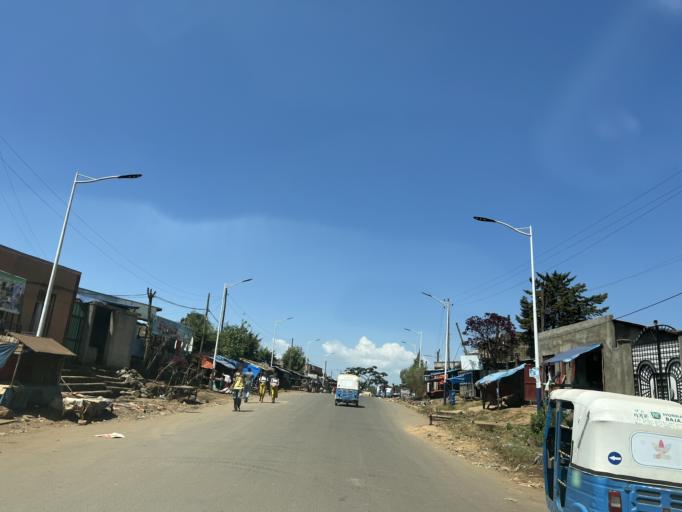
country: ET
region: Oromiya
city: Bedele
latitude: 9.0991
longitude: 36.5399
